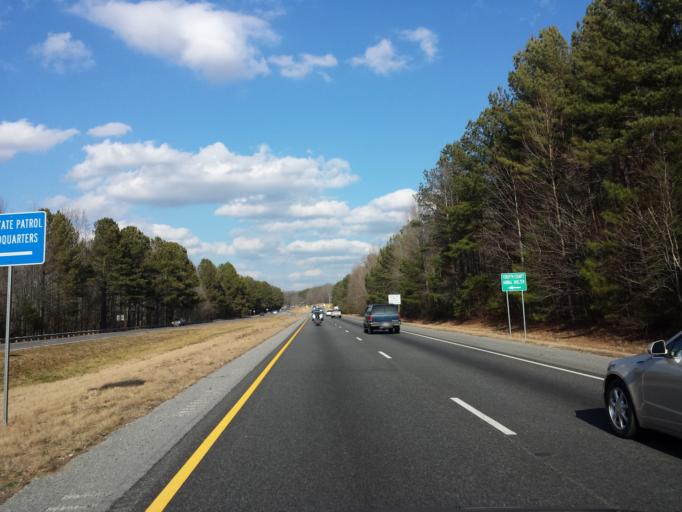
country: US
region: Georgia
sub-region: Forsyth County
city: Cumming
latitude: 34.2654
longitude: -84.0848
